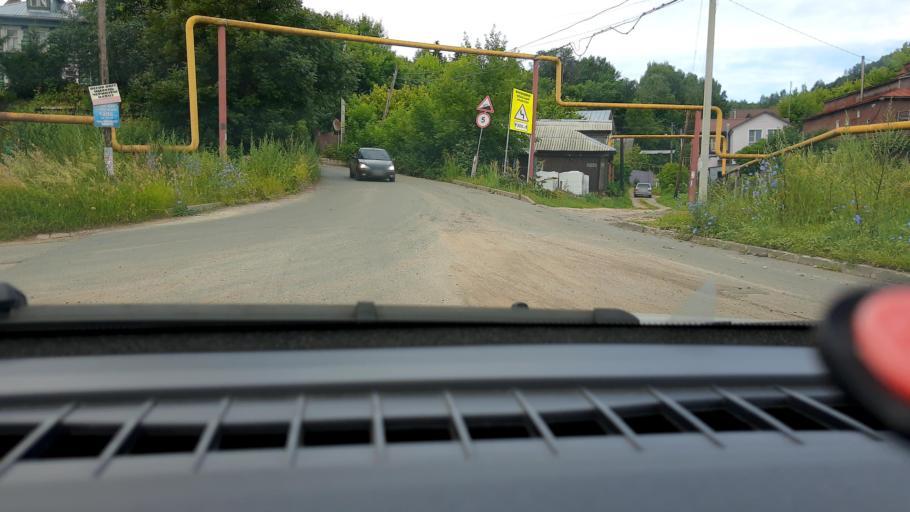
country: RU
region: Nizjnij Novgorod
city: Kstovo
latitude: 56.1498
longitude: 44.3438
